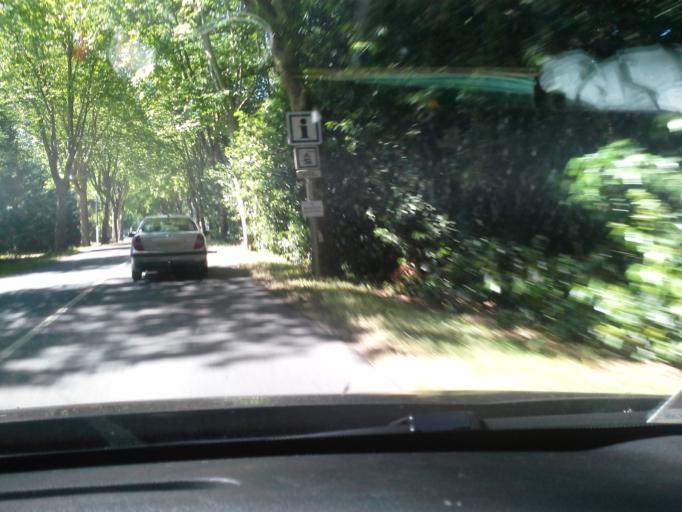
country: FR
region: Centre
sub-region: Departement du Loir-et-Cher
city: Cellettes
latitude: 47.5186
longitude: 1.3956
